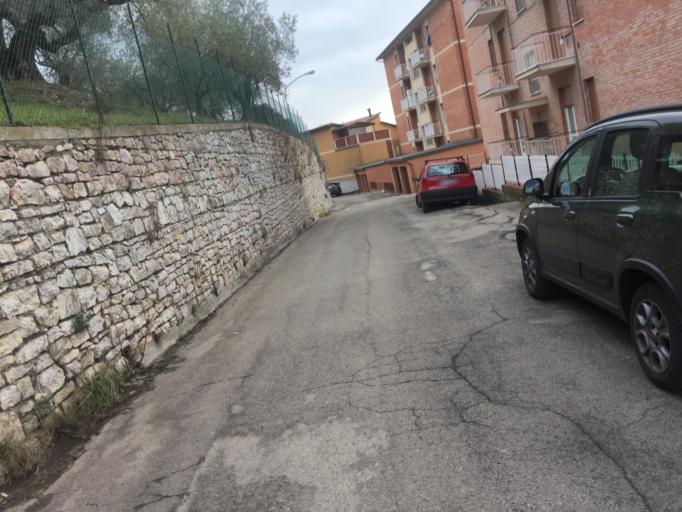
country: IT
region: Umbria
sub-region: Provincia di Perugia
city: Perugia
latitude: 43.1178
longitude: 12.4075
